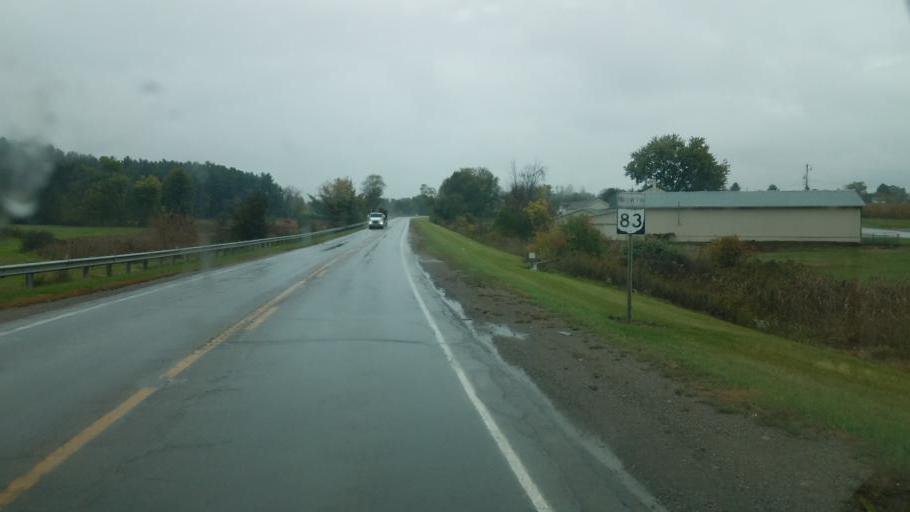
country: US
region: Ohio
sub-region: Holmes County
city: Millersburg
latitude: 40.6219
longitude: -81.9217
